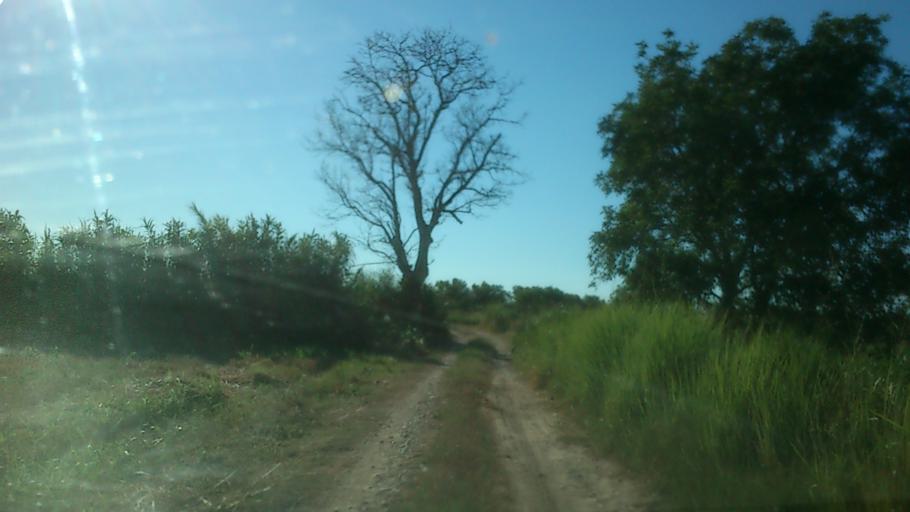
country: ES
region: Aragon
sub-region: Provincia de Zaragoza
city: Villanueva de Gallego
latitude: 41.7670
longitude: -0.8035
